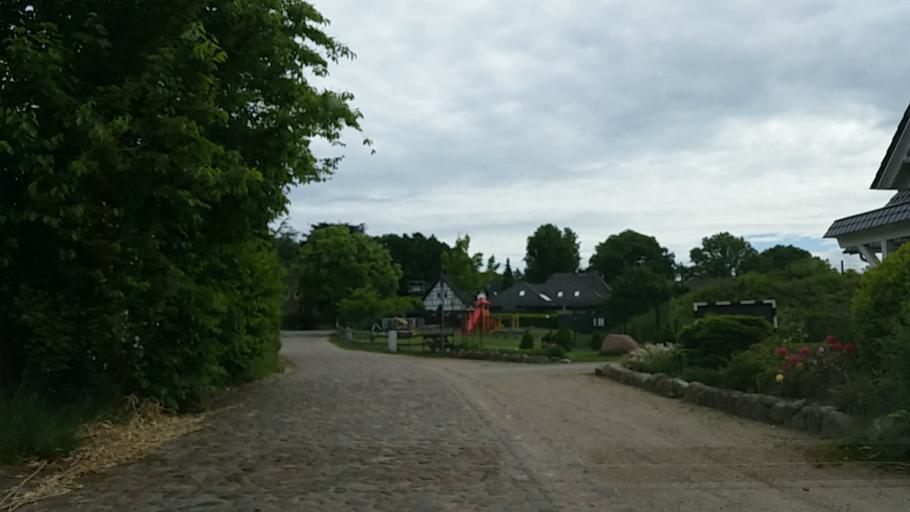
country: DE
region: Schleswig-Holstein
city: Dahmker
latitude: 53.6027
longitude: 10.4525
